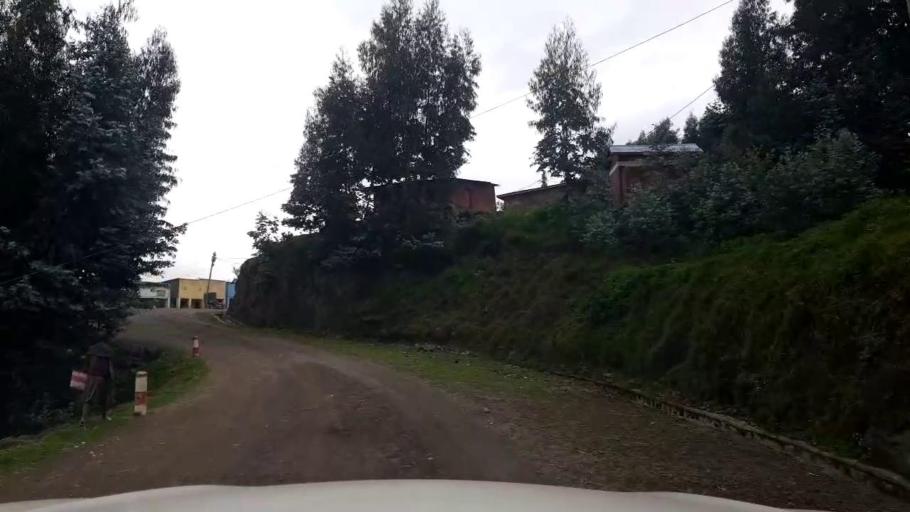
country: RW
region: Northern Province
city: Musanze
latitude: -1.5149
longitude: 29.5354
